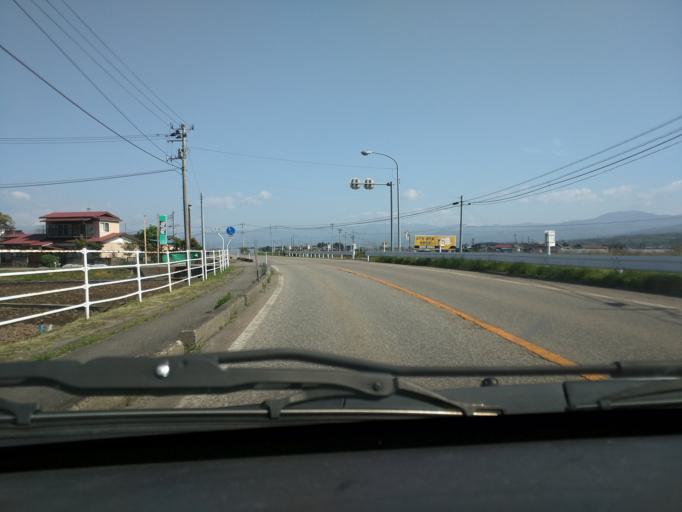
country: JP
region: Fukushima
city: Kitakata
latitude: 37.5609
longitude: 139.9067
